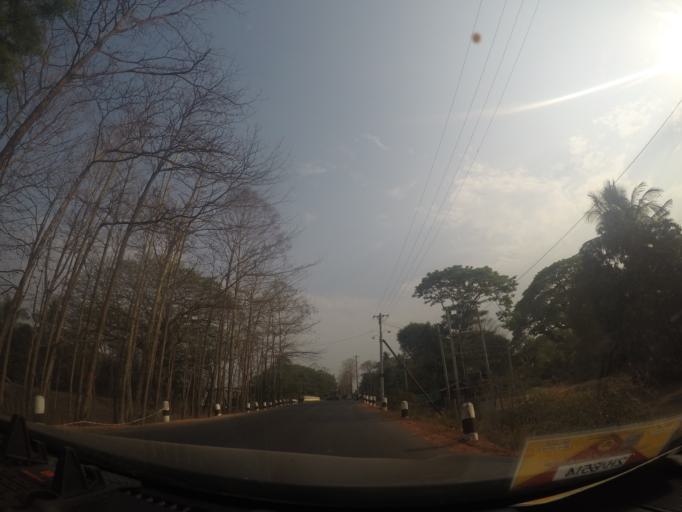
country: MM
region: Bago
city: Paungde
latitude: 18.3178
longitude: 95.6287
